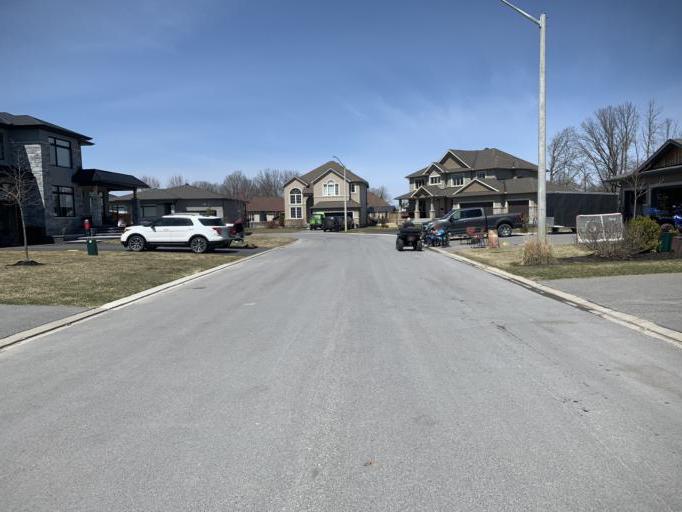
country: CA
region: Ontario
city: Bells Corners
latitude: 45.2005
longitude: -75.8375
